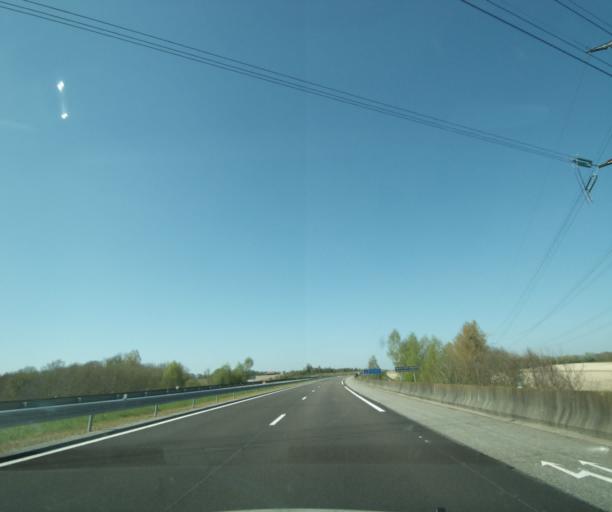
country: FR
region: Bourgogne
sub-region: Departement de la Nievre
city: Neuvy-sur-Loire
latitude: 47.5520
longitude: 2.8861
